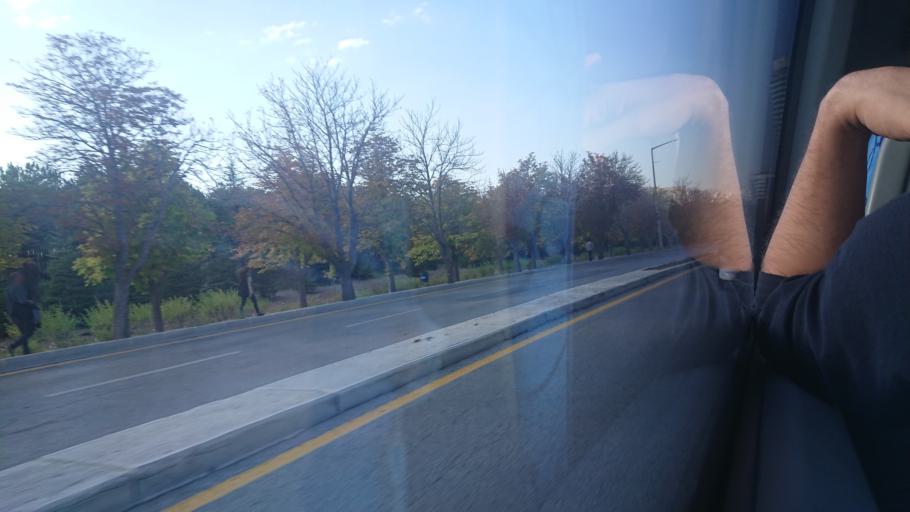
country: TR
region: Ankara
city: Ankara
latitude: 39.9047
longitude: 32.7833
